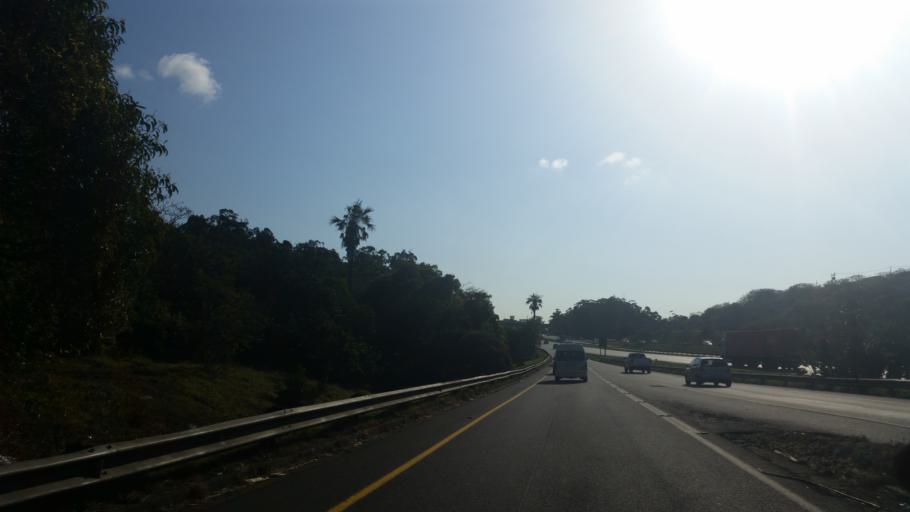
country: ZA
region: KwaZulu-Natal
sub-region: eThekwini Metropolitan Municipality
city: Berea
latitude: -29.8381
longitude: 30.9577
